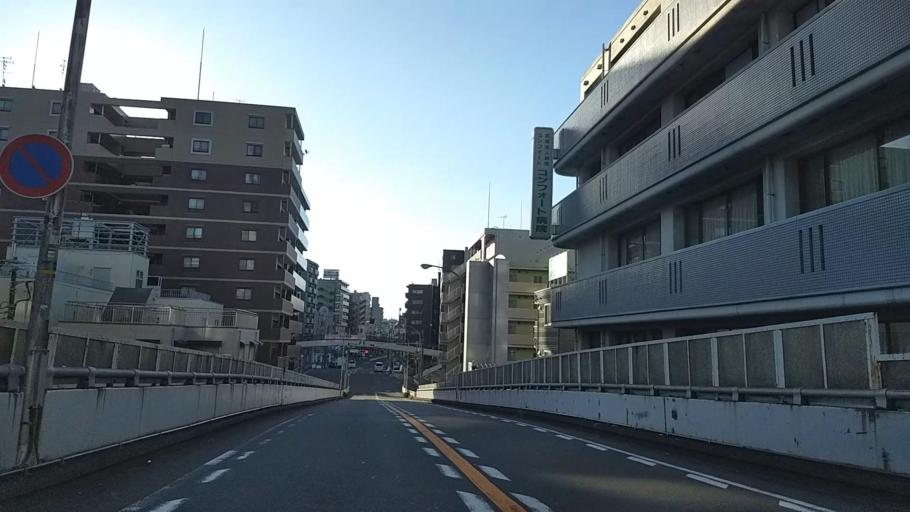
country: JP
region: Kanagawa
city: Yokohama
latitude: 35.4584
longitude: 139.6167
